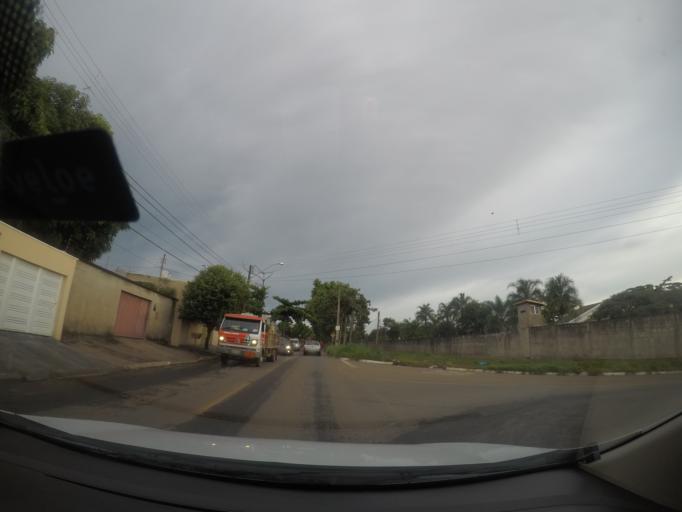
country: BR
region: Goias
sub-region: Goiania
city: Goiania
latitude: -16.7223
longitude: -49.3101
